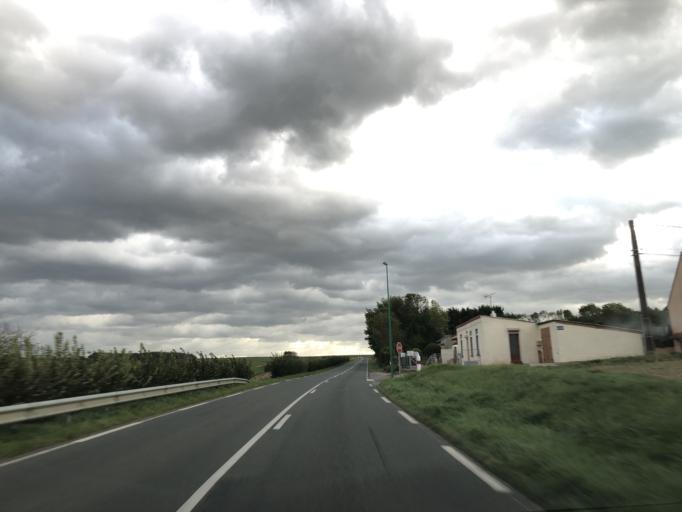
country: FR
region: Picardie
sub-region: Departement de la Somme
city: Ault
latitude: 50.1194
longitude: 1.4843
